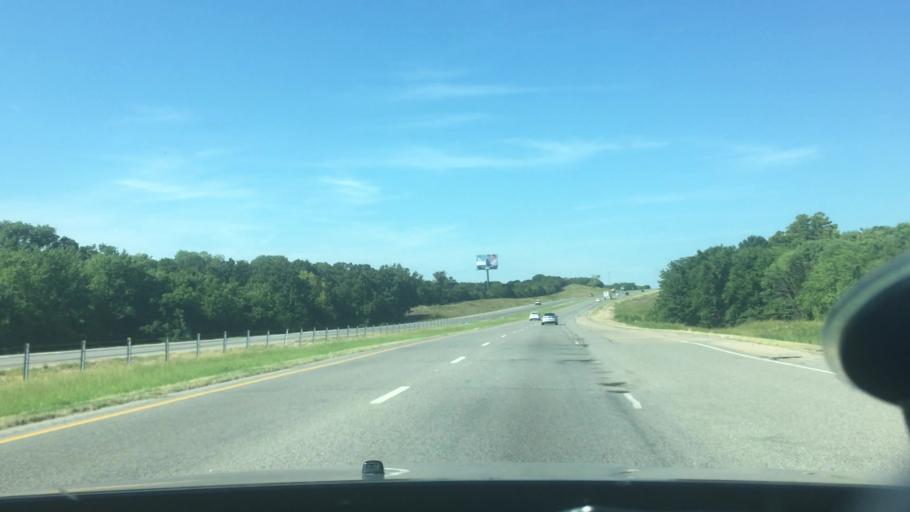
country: US
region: Oklahoma
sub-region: Bryan County
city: Durant
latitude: 34.0481
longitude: -96.3606
